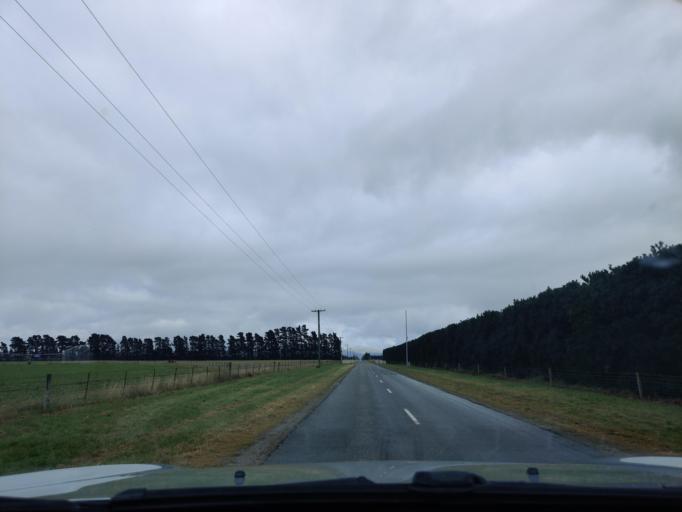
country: NZ
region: Canterbury
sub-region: Hurunui District
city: Amberley
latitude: -43.0779
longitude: 172.7317
